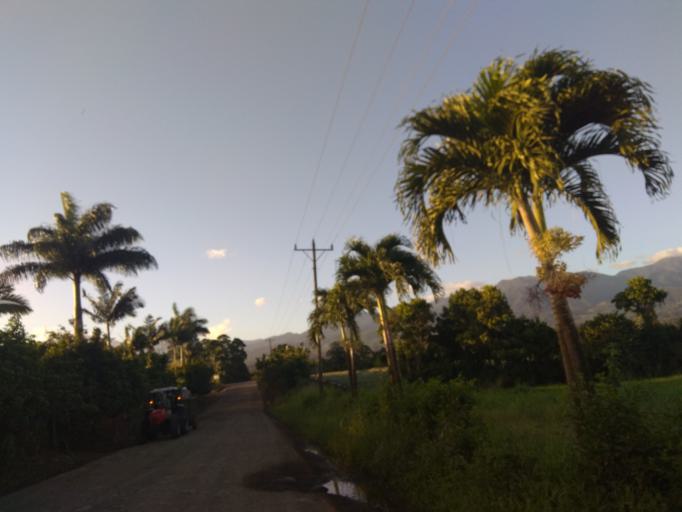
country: CR
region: Alajuela
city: Pital
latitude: 10.3877
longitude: -84.2636
